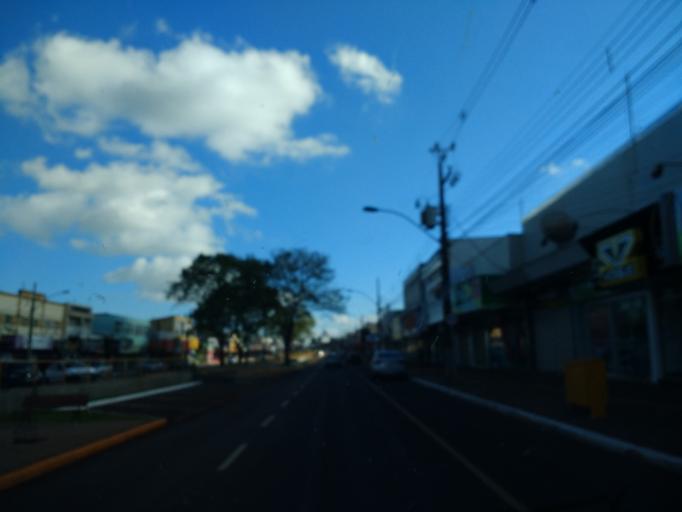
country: BR
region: Parana
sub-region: Palotina
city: Palotina
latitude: -24.4082
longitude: -53.5170
